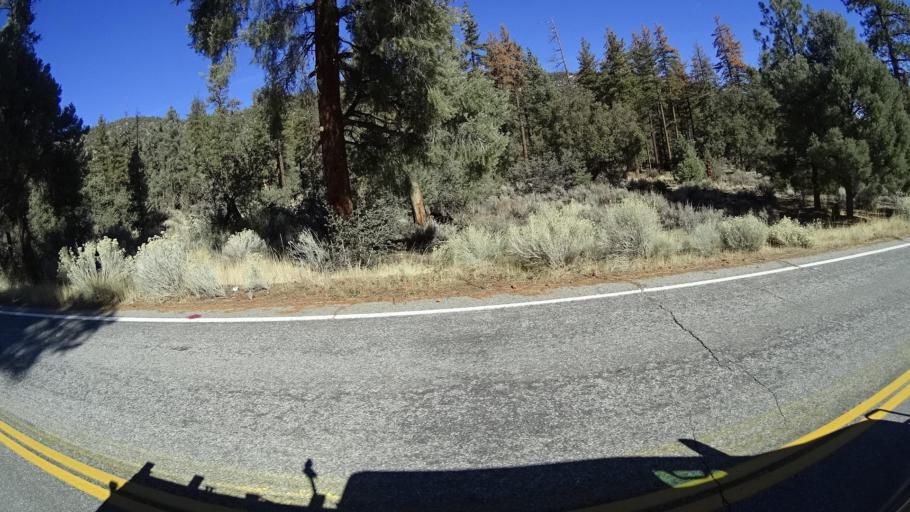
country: US
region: California
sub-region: Kern County
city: Pine Mountain Club
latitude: 34.8570
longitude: -119.1966
